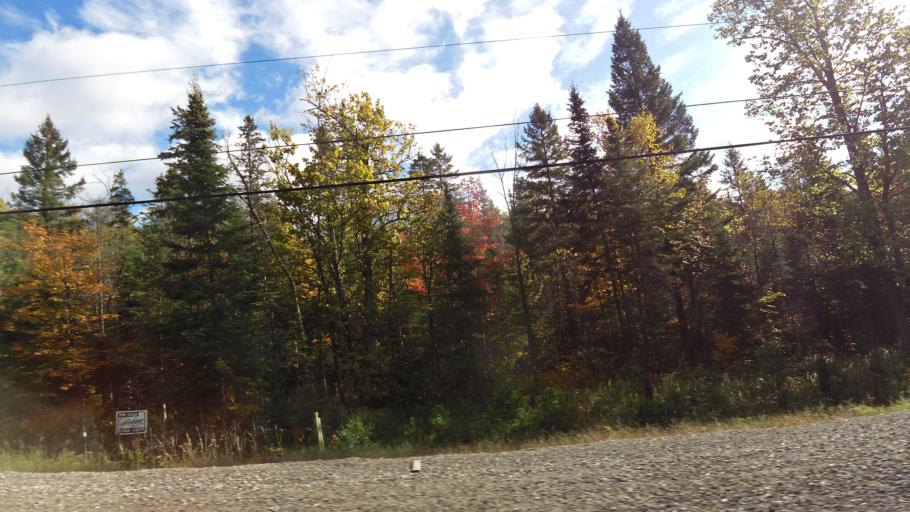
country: CA
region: Ontario
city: Deep River
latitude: 46.0698
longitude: -77.4755
